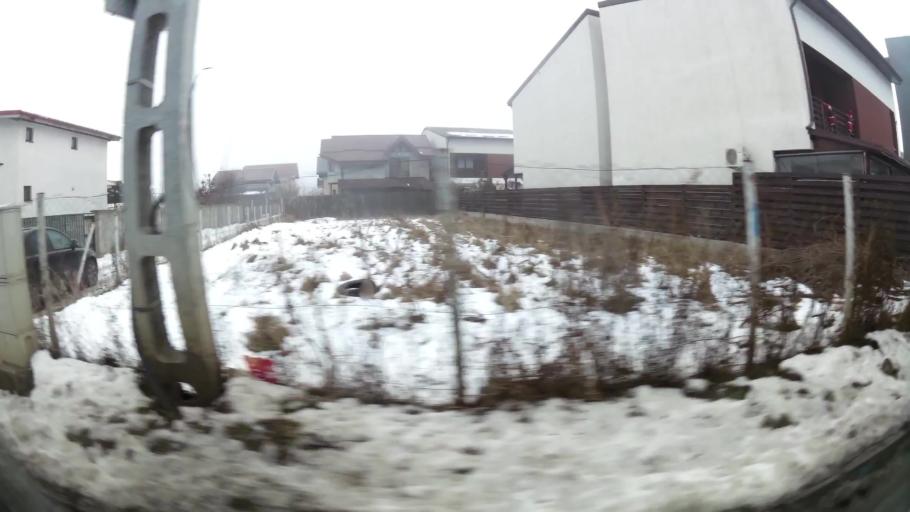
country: RO
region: Ilfov
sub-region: Comuna Chiajna
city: Chiajna
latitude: 44.4530
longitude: 25.9847
